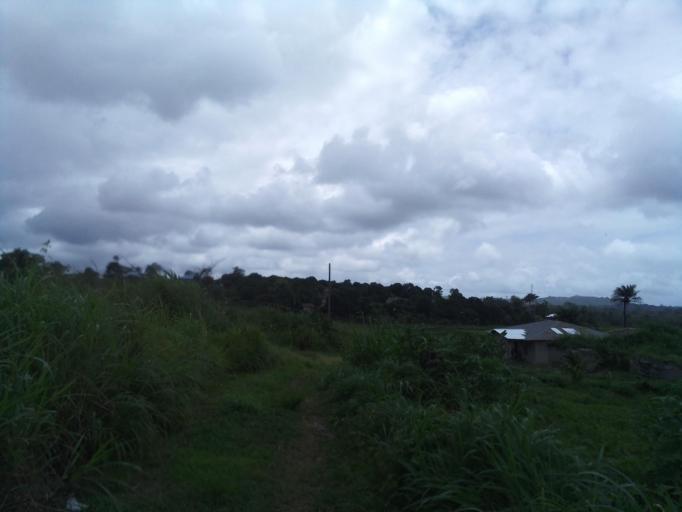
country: SL
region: Eastern Province
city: Kenema
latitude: 7.8319
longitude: -11.1804
